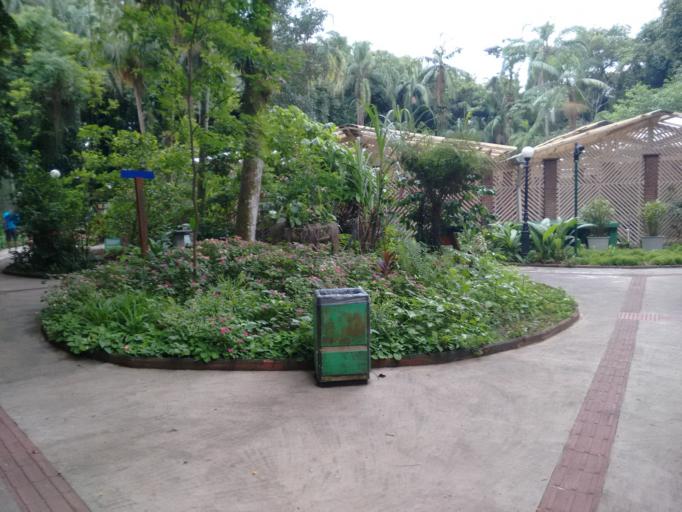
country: BR
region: Sao Paulo
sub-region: Santos
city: Santos
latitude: -23.9664
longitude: -46.3501
